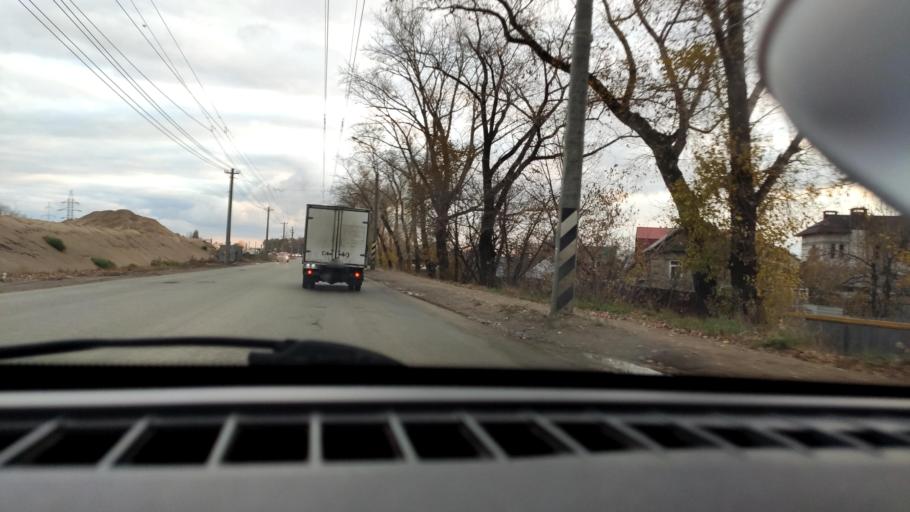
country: RU
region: Samara
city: Samara
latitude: 53.1451
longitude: 50.0967
